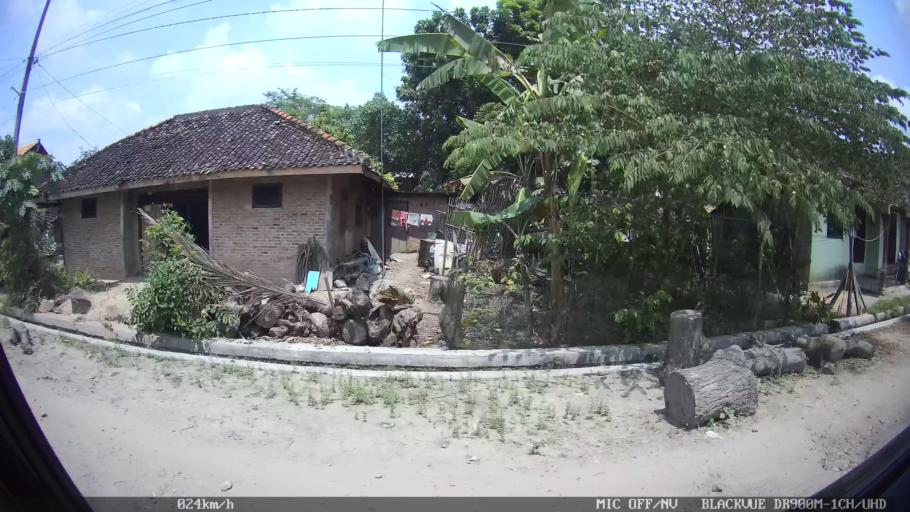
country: ID
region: Lampung
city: Pringsewu
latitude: -5.3448
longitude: 104.9860
